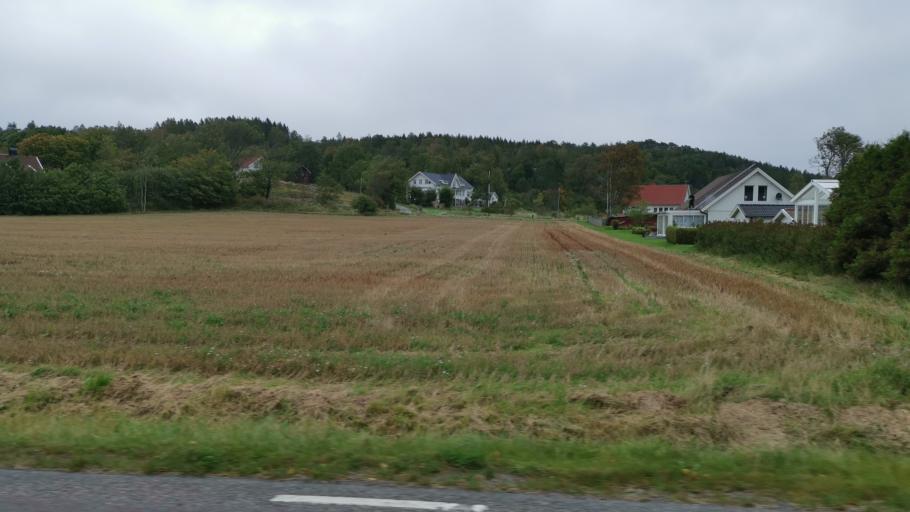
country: SE
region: Vaestra Goetaland
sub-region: Sotenas Kommun
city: Hunnebostrand
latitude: 58.5665
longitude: 11.3742
